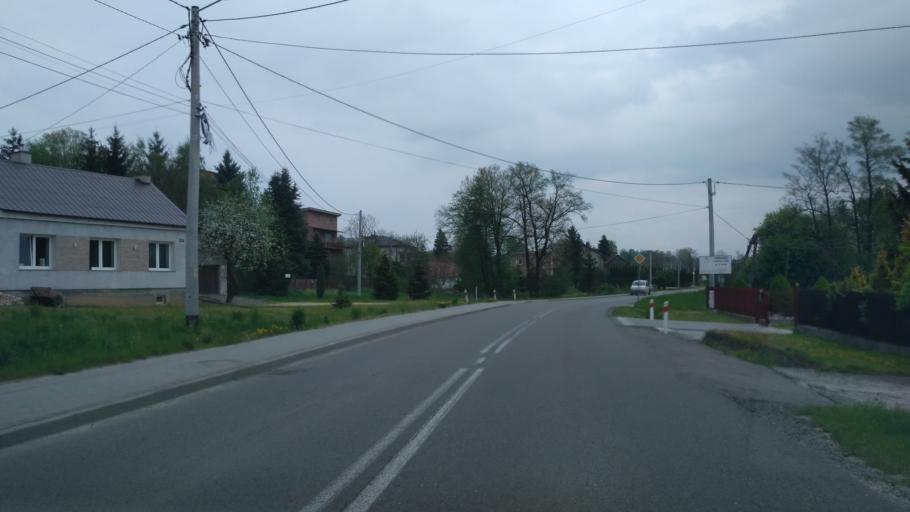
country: PL
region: Lesser Poland Voivodeship
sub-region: Powiat tarnowski
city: Skrzyszow
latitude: 49.9872
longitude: 21.0906
